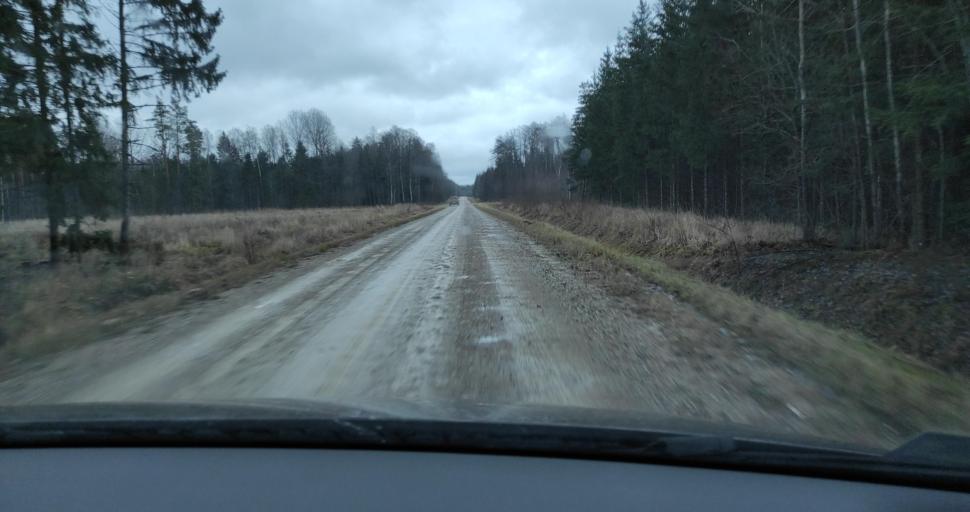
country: LV
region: Skrunda
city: Skrunda
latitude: 56.5578
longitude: 22.1084
